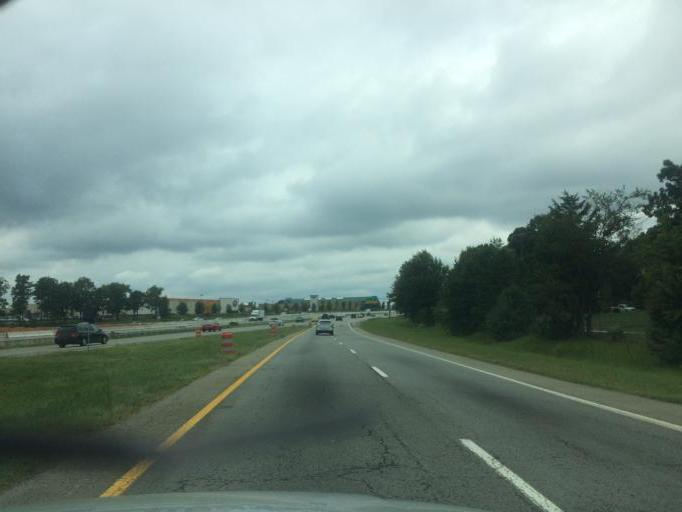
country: US
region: South Carolina
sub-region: Greenville County
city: Mauldin
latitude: 34.8348
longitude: -82.3001
